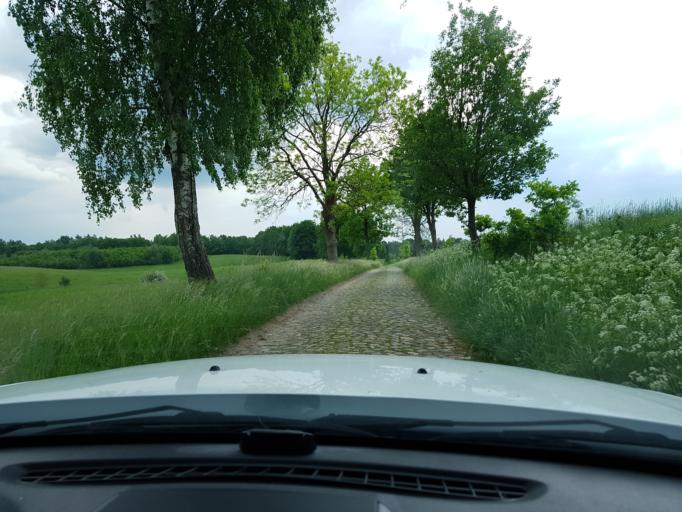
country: PL
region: West Pomeranian Voivodeship
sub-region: Powiat drawski
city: Drawsko Pomorskie
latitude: 53.5504
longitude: 15.7249
